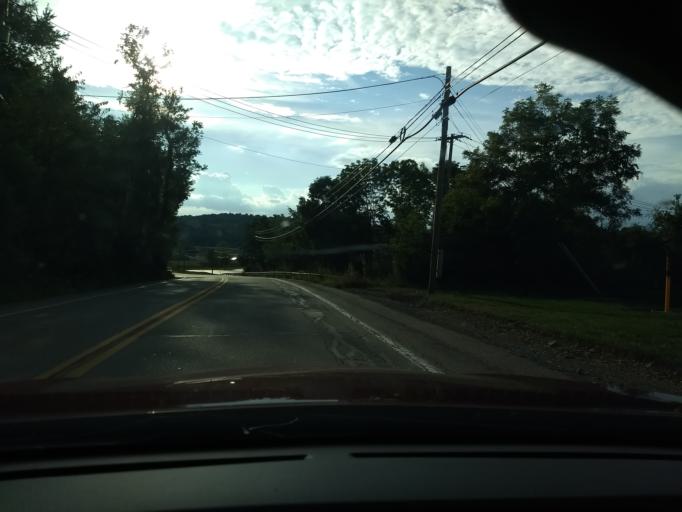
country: US
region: Pennsylvania
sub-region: Armstrong County
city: Freeport
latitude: 40.6672
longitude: -79.7070
